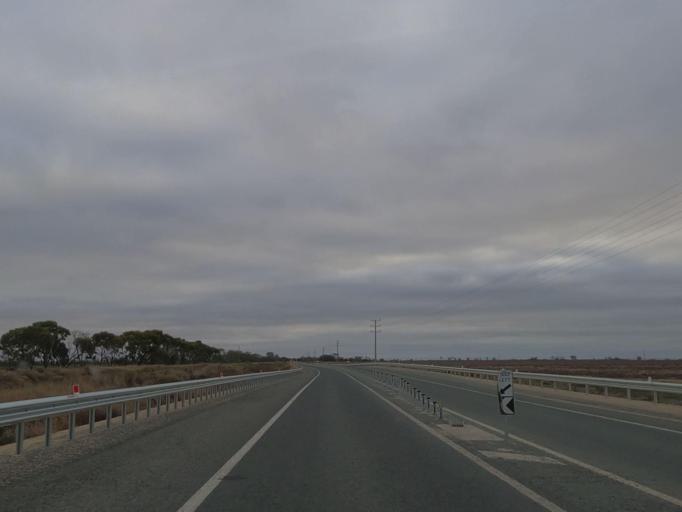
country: AU
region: Victoria
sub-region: Swan Hill
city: Swan Hill
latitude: -35.5442
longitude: 143.7580
